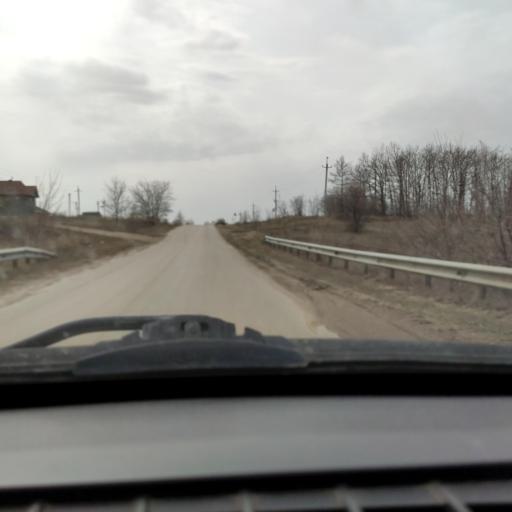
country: RU
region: Samara
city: Dubovyy Umet
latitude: 53.0419
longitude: 50.1773
